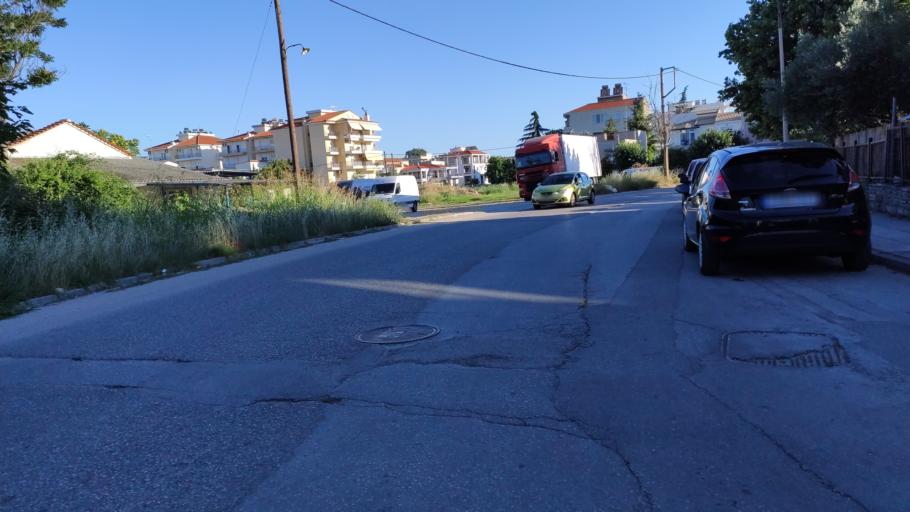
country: GR
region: East Macedonia and Thrace
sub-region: Nomos Rodopis
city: Komotini
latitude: 41.1237
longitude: 25.3947
